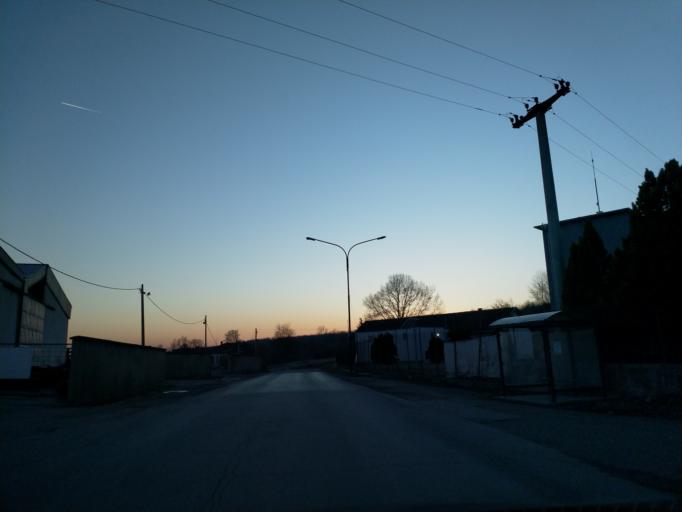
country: RS
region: Central Serbia
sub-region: Pomoravski Okrug
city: Paracin
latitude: 43.9038
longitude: 21.4971
